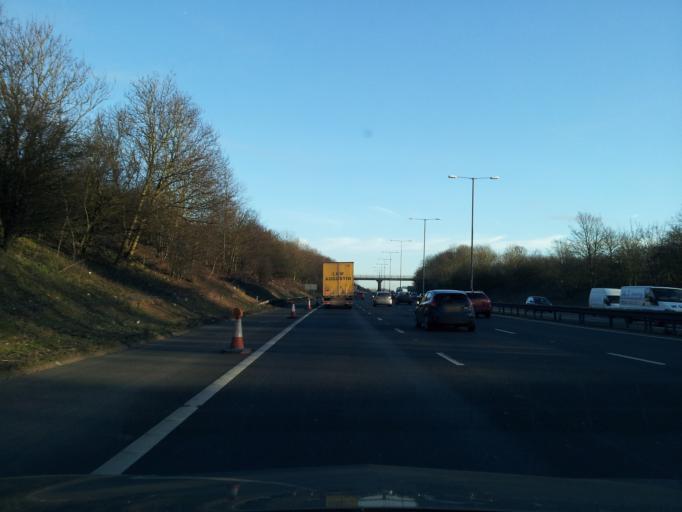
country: GB
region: England
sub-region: Northamptonshire
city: Blisworth
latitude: 52.2022
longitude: -0.9217
